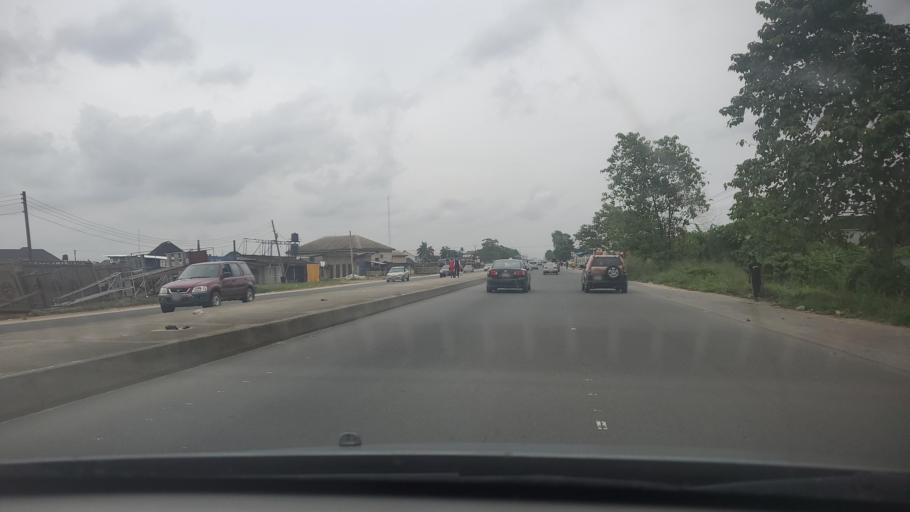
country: NG
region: Rivers
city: Port Harcourt
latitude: 4.8709
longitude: 6.9672
